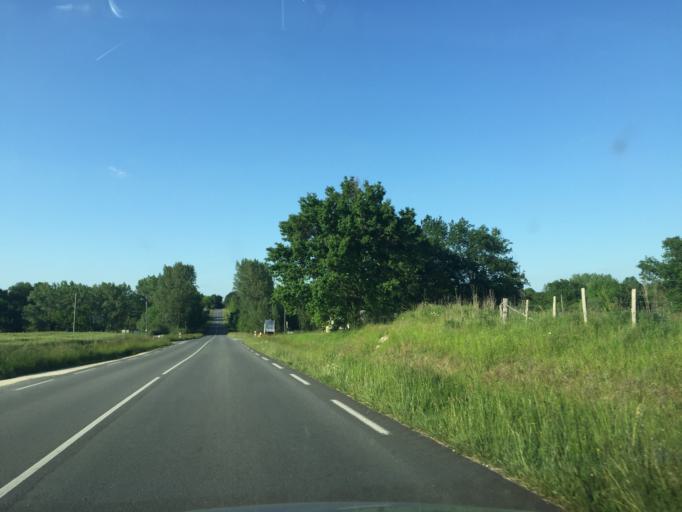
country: FR
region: Aquitaine
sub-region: Departement de la Dordogne
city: La Roche-Chalais
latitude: 45.1953
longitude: 0.0323
